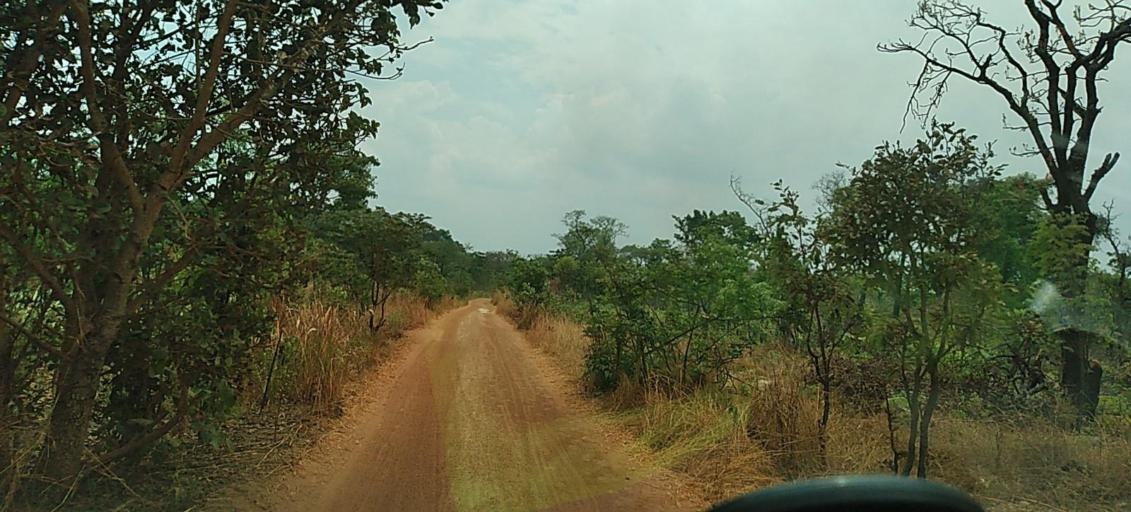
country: ZM
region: North-Western
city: Kansanshi
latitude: -12.0381
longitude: 26.3228
